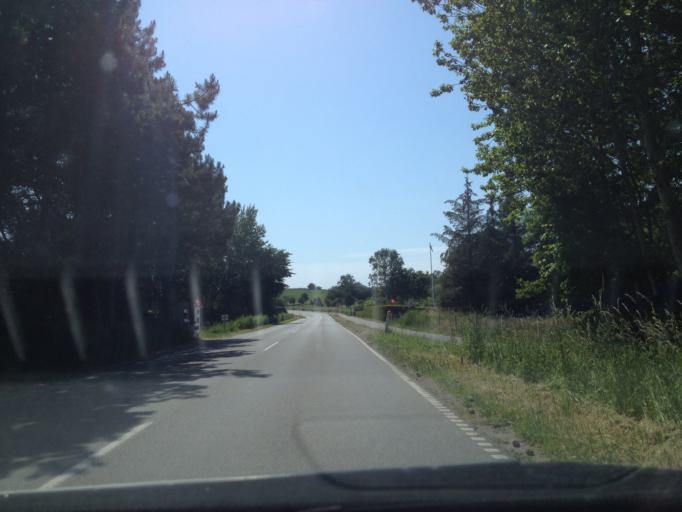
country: DK
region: Central Jutland
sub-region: Samso Kommune
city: Tranebjerg
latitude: 55.8613
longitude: 10.5753
